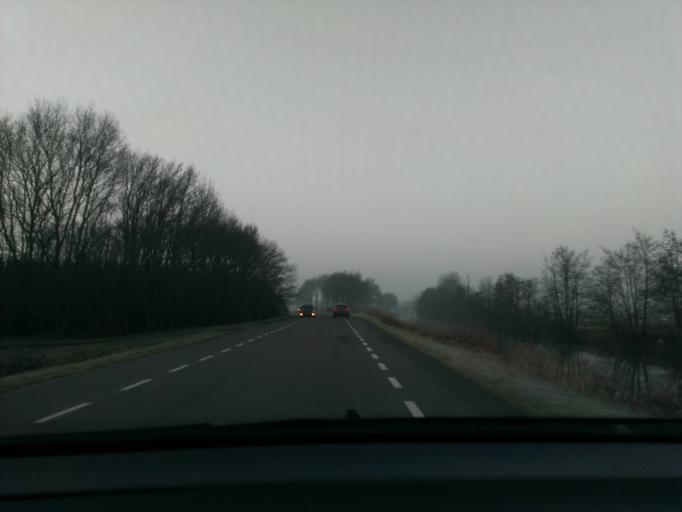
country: NL
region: Gelderland
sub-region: Gemeente Epe
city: Emst
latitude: 52.3182
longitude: 6.0110
